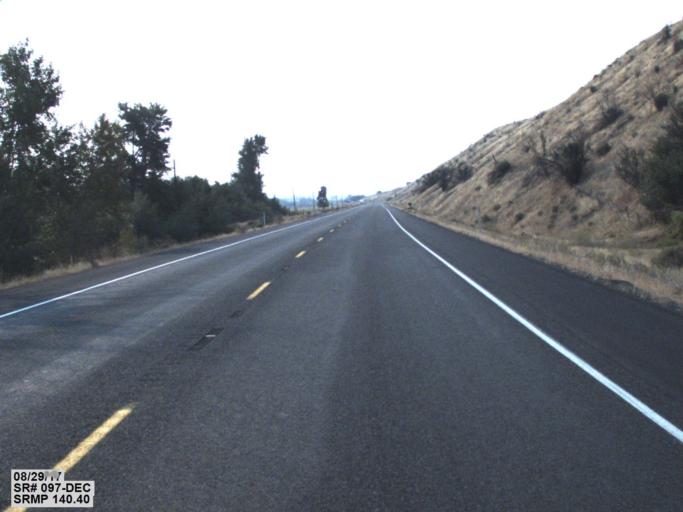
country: US
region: Washington
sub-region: Kittitas County
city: Ellensburg
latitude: 47.0835
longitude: -120.6424
